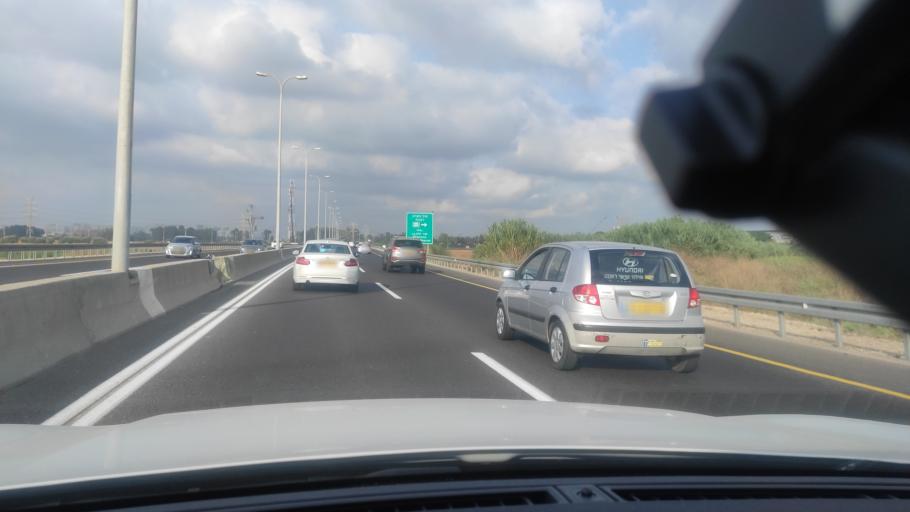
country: IL
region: Central District
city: Hod HaSharon
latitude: 32.1323
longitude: 34.9074
